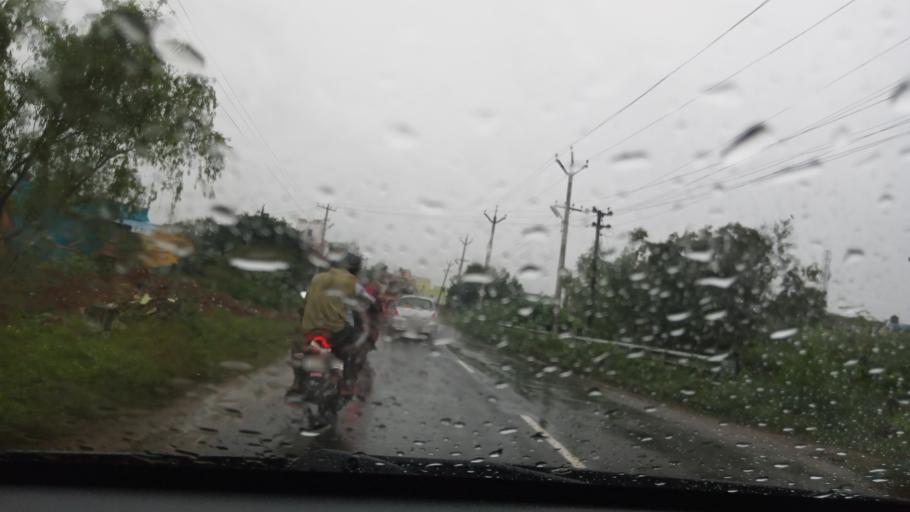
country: IN
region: Tamil Nadu
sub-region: Tiruvannamalai
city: Cheyyar
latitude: 12.6682
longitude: 79.5365
